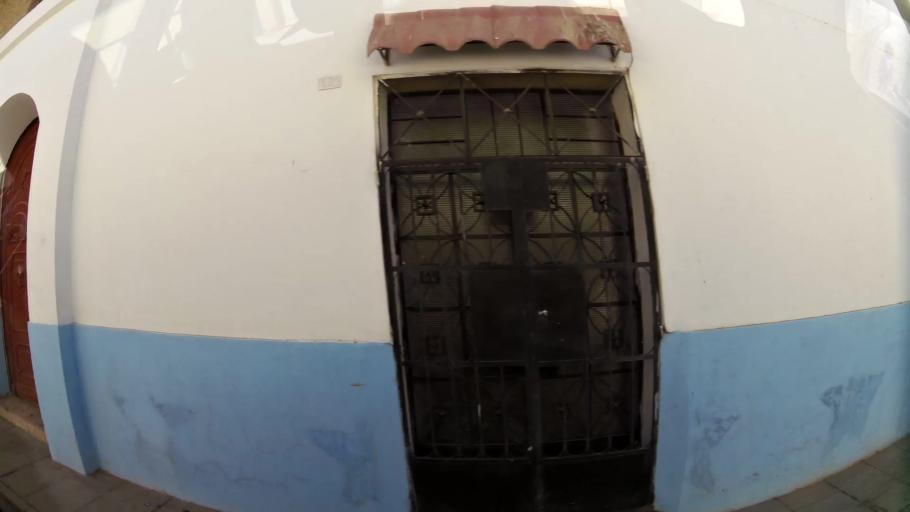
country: PE
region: Junin
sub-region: Provincia de Concepcion
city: Concepcion
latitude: -11.9200
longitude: -75.3117
